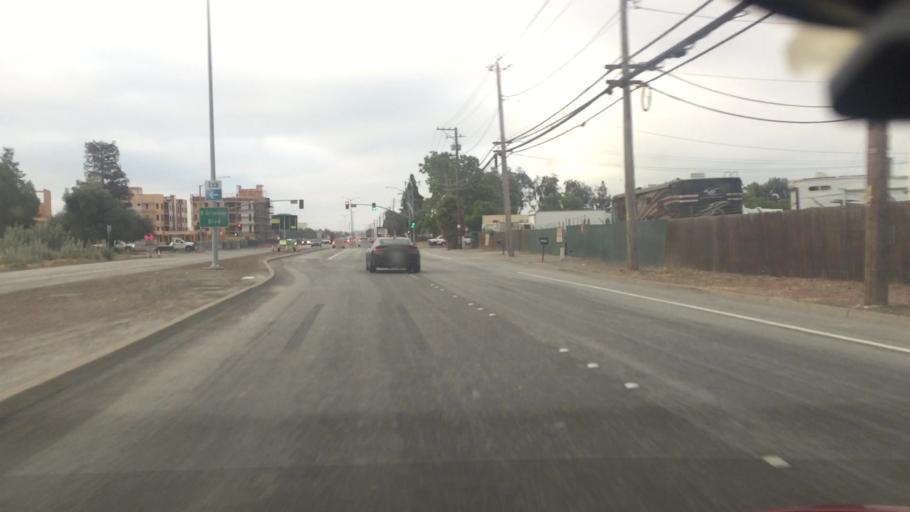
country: US
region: California
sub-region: Alameda County
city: Fremont
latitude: 37.5038
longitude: -121.9492
